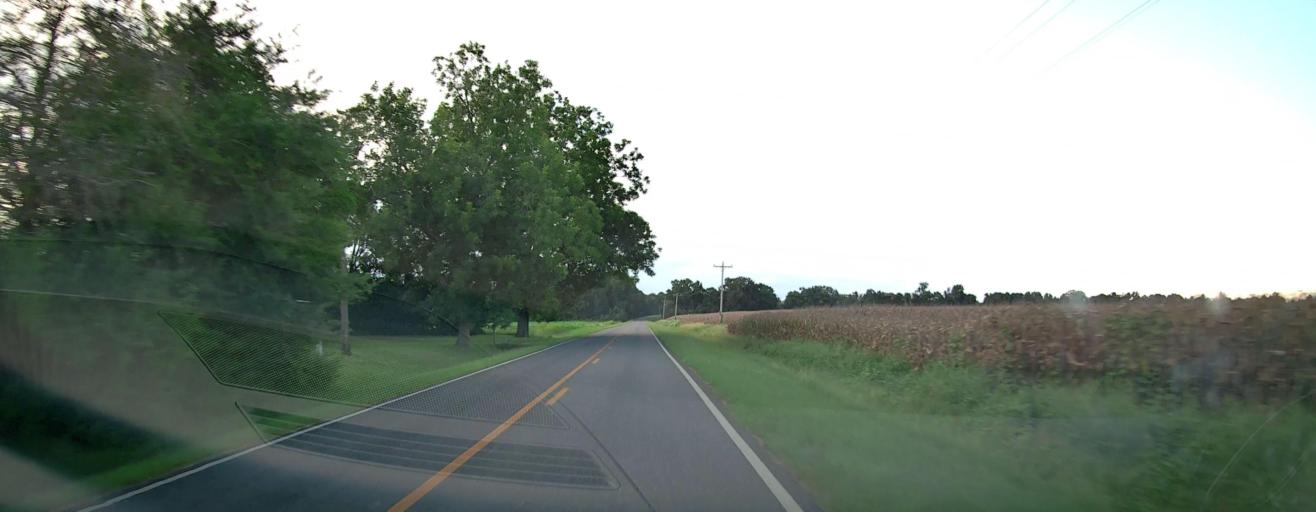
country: US
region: Georgia
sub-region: Pulaski County
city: Hawkinsville
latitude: 32.3062
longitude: -83.5529
